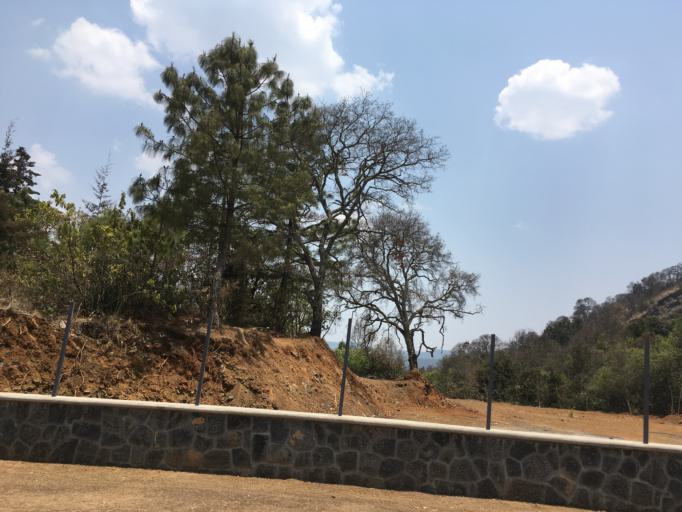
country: MX
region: Michoacan
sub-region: Patzcuaro
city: Santa Ana Chapitiro
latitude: 19.5147
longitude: -101.6370
